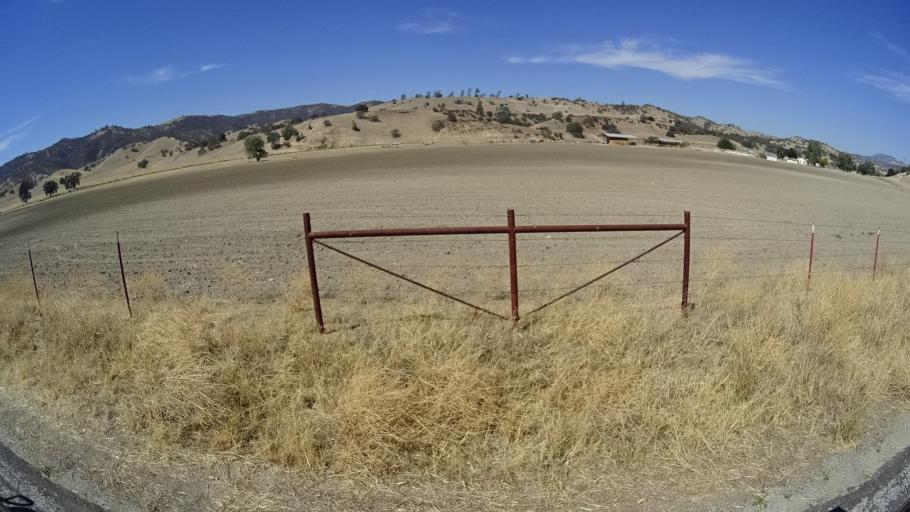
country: US
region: California
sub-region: San Luis Obispo County
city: San Miguel
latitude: 35.9520
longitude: -120.6552
